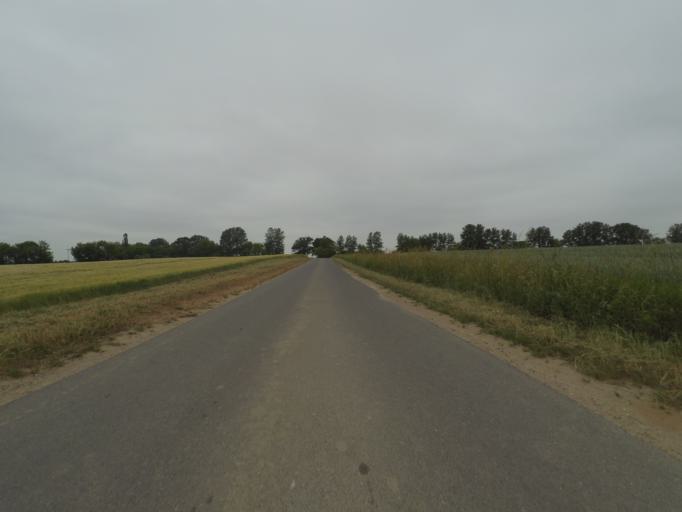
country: DE
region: Mecklenburg-Vorpommern
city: Goldberg
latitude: 53.5545
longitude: 12.0300
